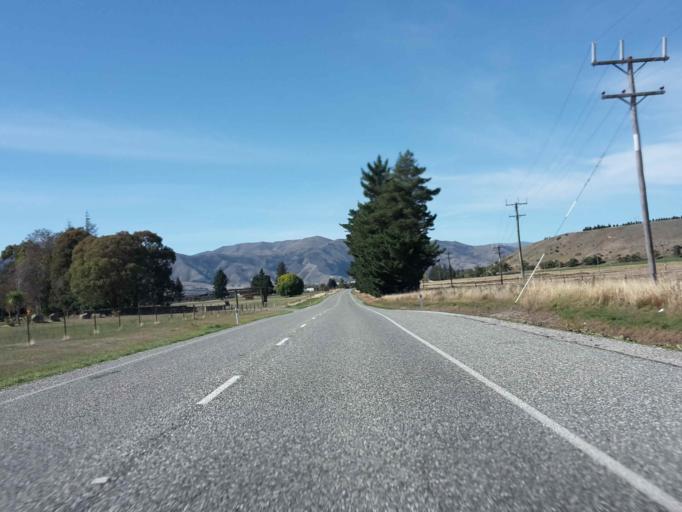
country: NZ
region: Otago
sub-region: Queenstown-Lakes District
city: Wanaka
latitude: -44.7206
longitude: 169.2286
